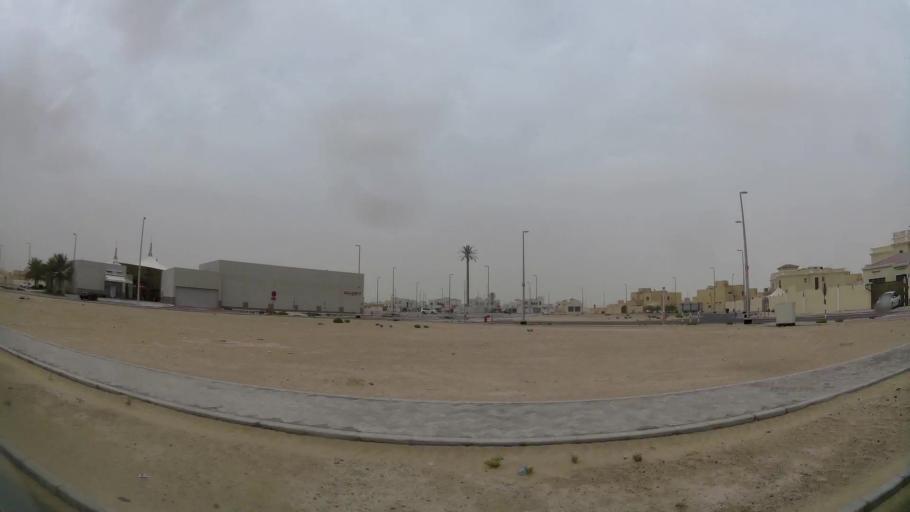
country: AE
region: Abu Dhabi
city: Abu Dhabi
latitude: 24.4443
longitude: 54.7406
